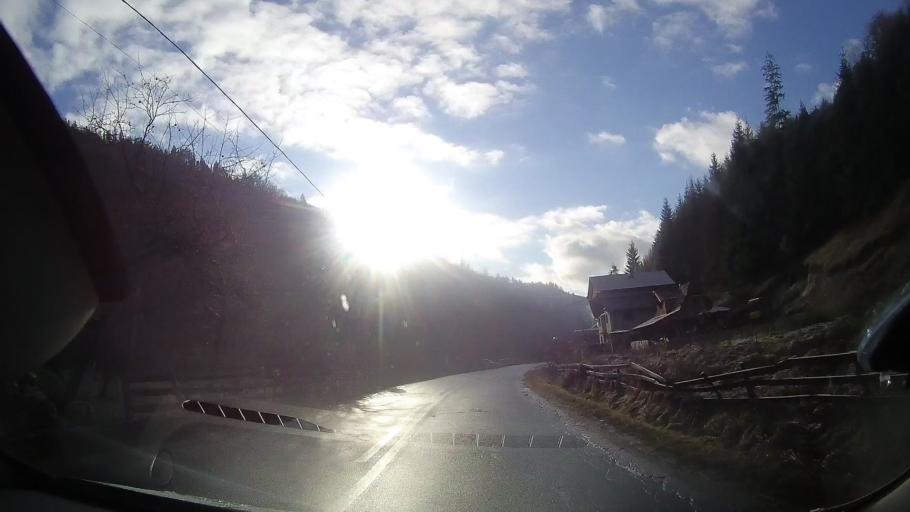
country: RO
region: Alba
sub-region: Comuna Albac
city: Albac
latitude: 46.4407
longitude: 22.9672
